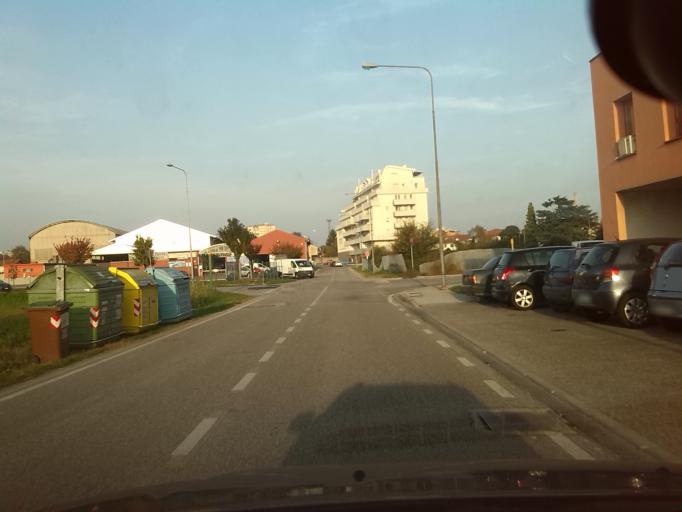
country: IT
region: Friuli Venezia Giulia
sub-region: Provincia di Udine
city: Basaldella
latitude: 46.0487
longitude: 13.2226
